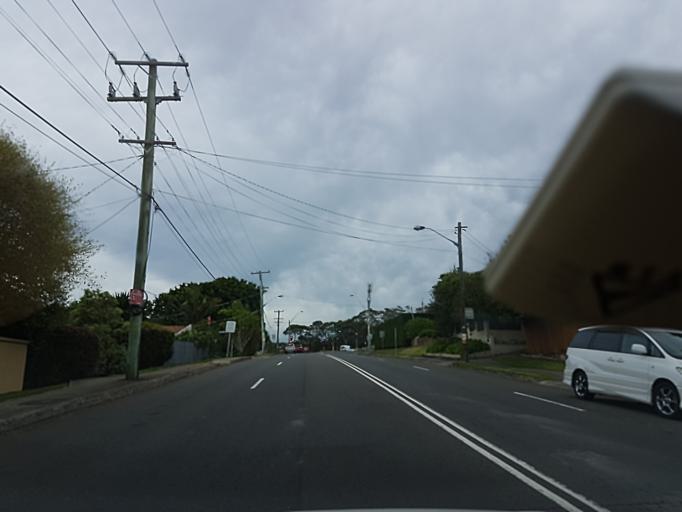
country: AU
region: New South Wales
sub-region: Warringah
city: Brookvale
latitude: -33.7562
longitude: 151.2640
